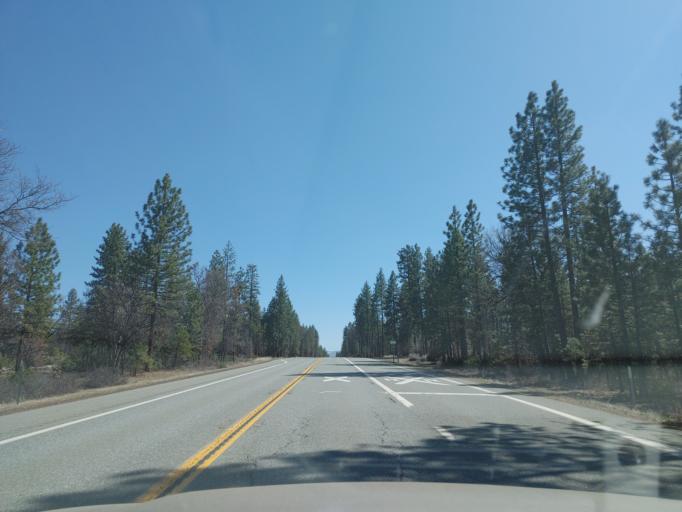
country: US
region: California
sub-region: Shasta County
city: Burney
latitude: 40.9710
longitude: -121.6195
